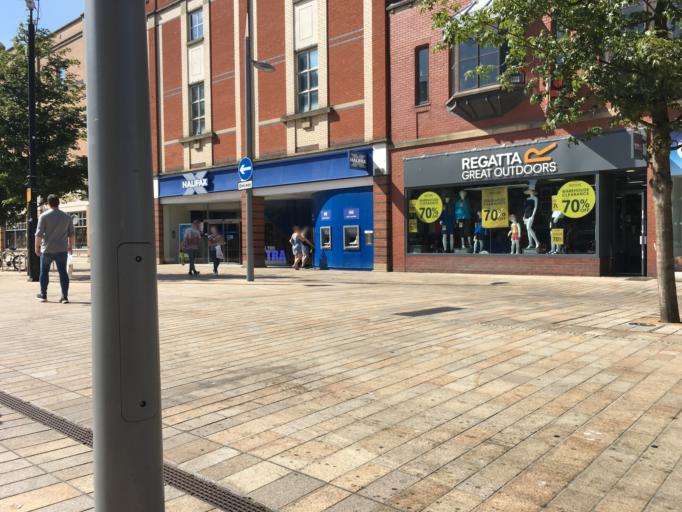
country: GB
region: England
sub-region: City of Kingston upon Hull
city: Hull
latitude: 53.7448
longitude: -0.3418
